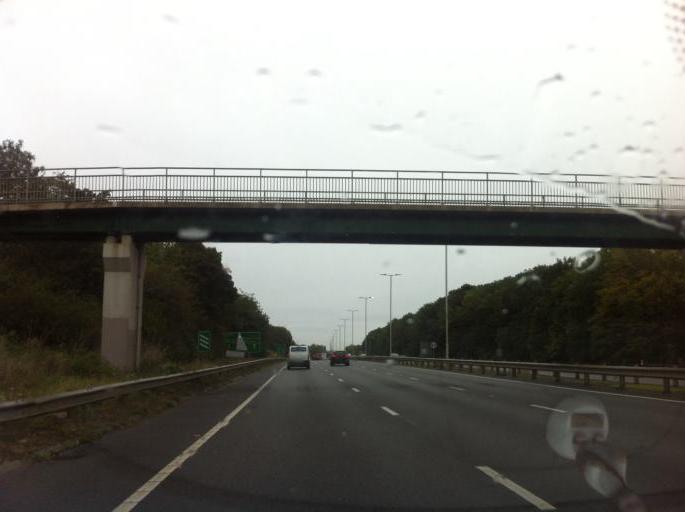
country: GB
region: England
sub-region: Cambridgeshire
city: Yaxley
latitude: 52.5437
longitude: -0.2758
